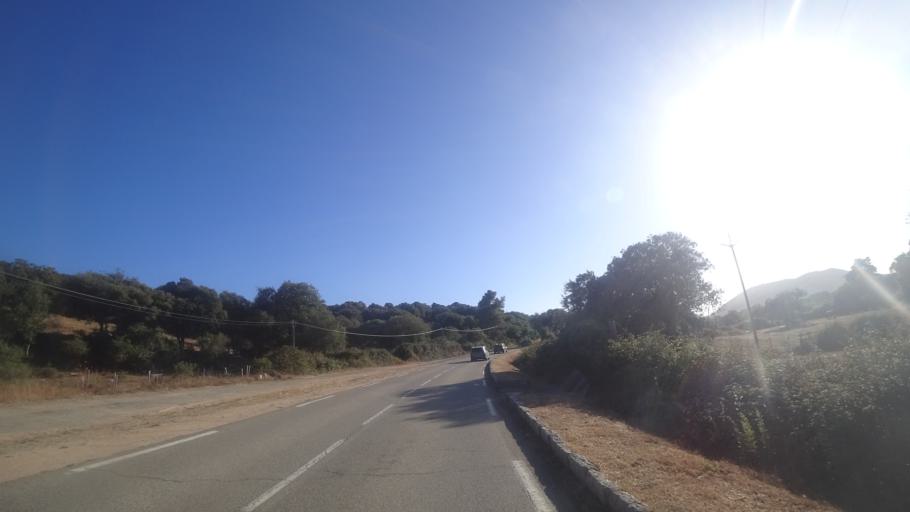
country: FR
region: Corsica
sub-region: Departement de la Corse-du-Sud
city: Cargese
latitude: 42.1734
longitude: 8.6107
